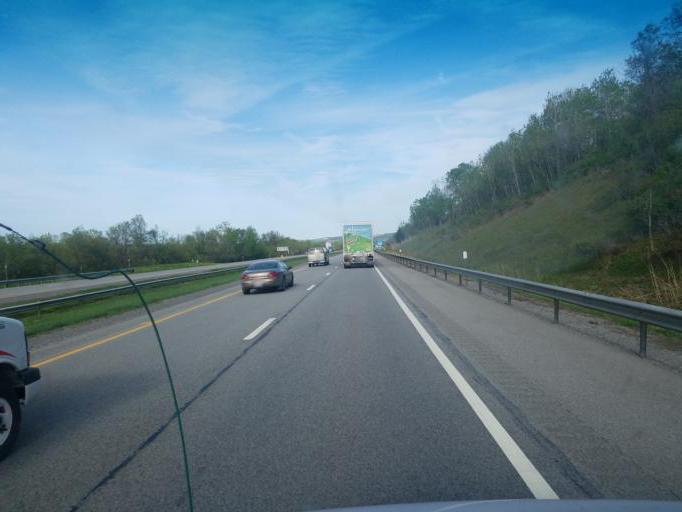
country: US
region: New York
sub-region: Herkimer County
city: Herkimer
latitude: 43.0144
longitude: -74.9600
